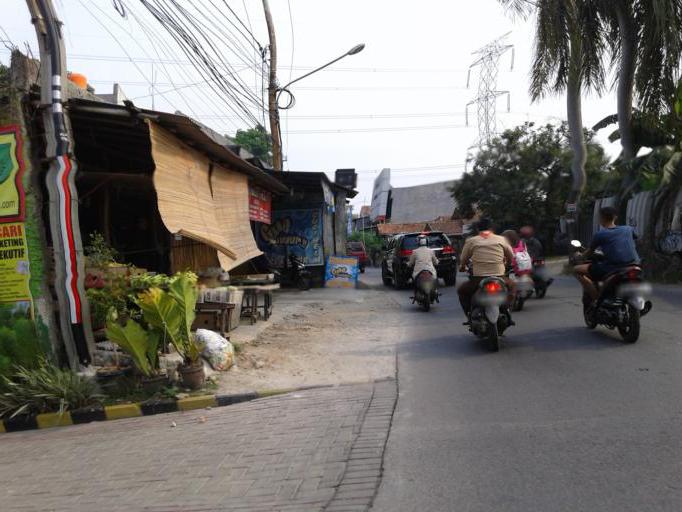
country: ID
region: West Java
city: Pamulang
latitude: -6.3576
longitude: 106.7756
